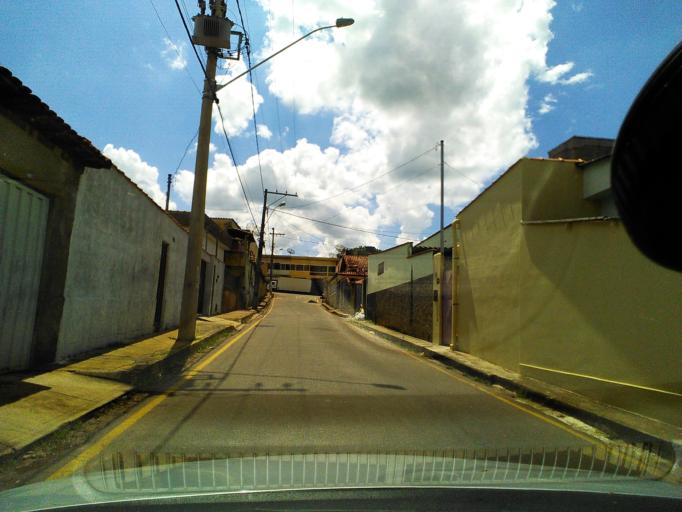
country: BR
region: Minas Gerais
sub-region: Tres Coracoes
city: Tres Coracoes
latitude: -21.7218
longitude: -45.2617
